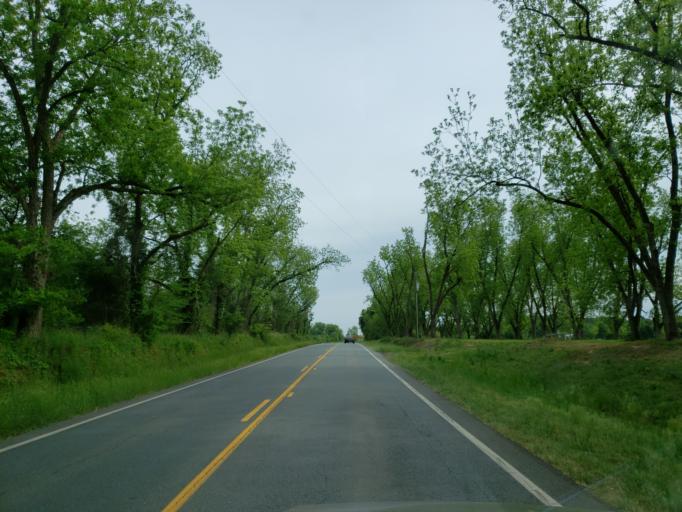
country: US
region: Georgia
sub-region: Macon County
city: Marshallville
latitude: 32.3933
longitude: -83.8669
